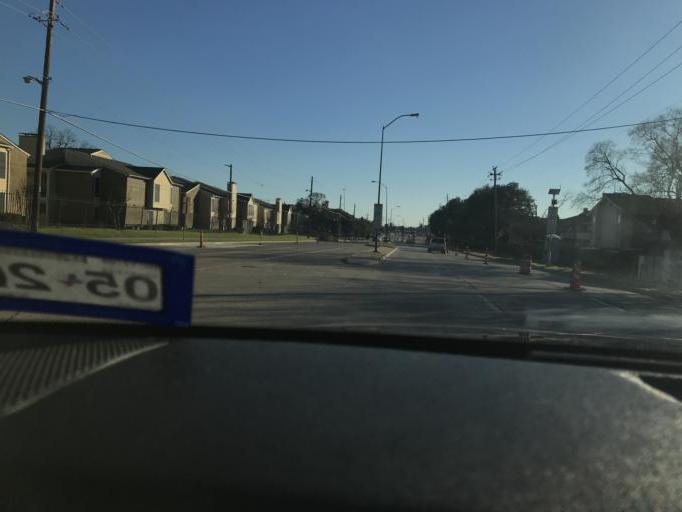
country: US
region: Texas
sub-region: Dallas County
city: Richardson
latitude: 32.9157
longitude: -96.7355
